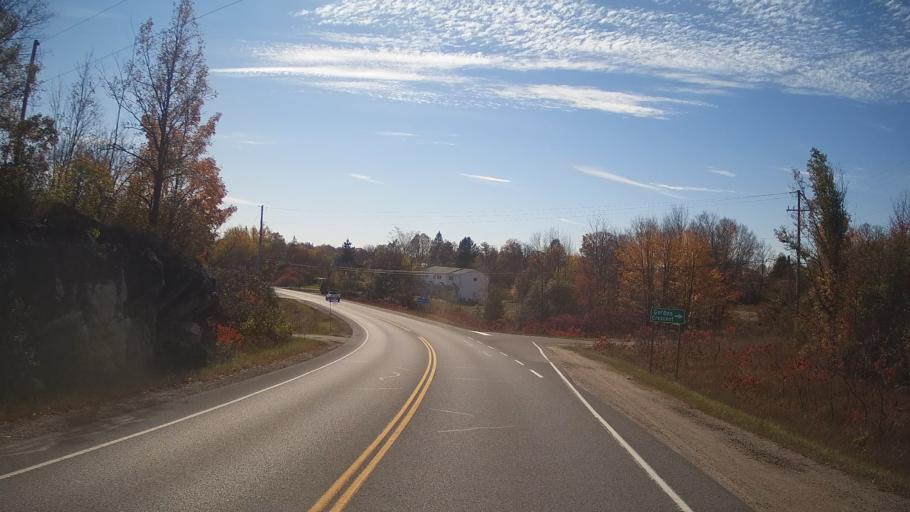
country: CA
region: Ontario
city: Perth
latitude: 44.7831
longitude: -76.6816
